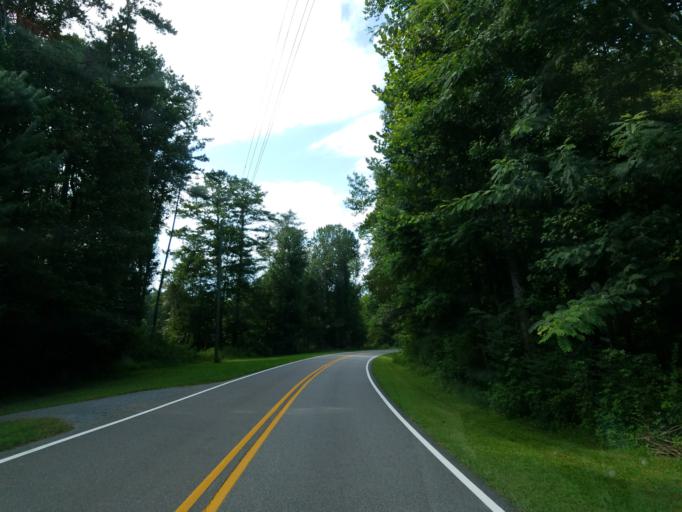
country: US
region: Georgia
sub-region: Gilmer County
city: Ellijay
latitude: 34.7803
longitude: -84.4250
